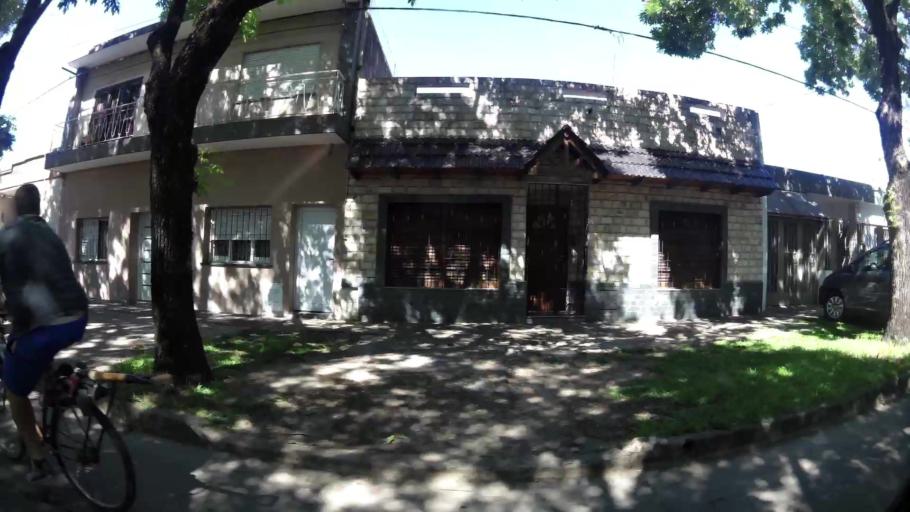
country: AR
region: Santa Fe
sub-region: Departamento de Rosario
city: Rosario
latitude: -32.9373
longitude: -60.6946
